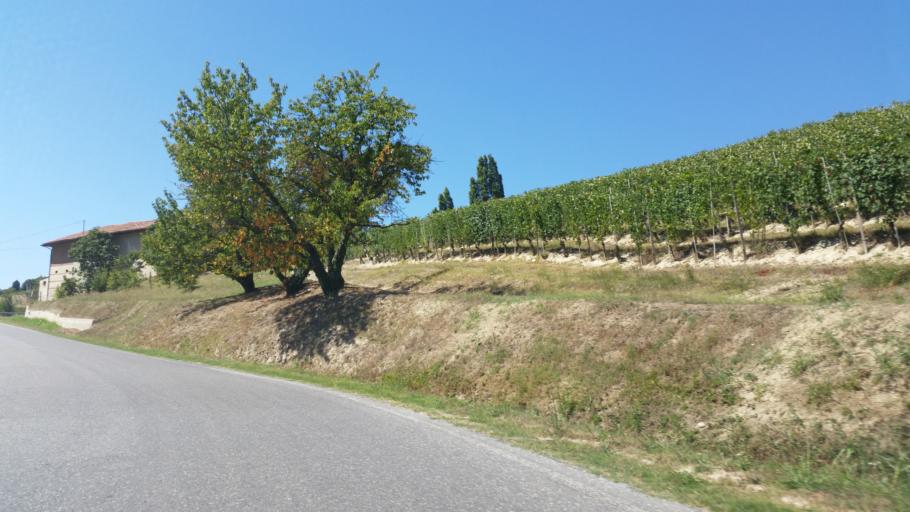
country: IT
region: Piedmont
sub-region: Provincia di Cuneo
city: Barbaresco
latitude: 44.7061
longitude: 8.0660
